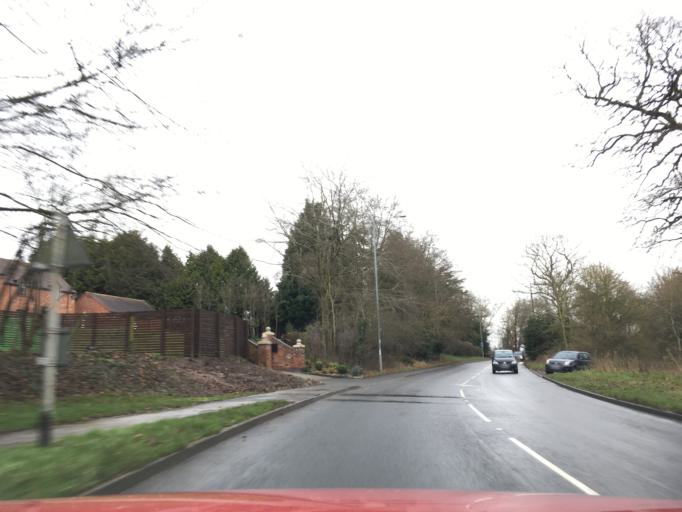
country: GB
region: England
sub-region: Warwickshire
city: Alcester
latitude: 52.2100
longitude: -1.8791
